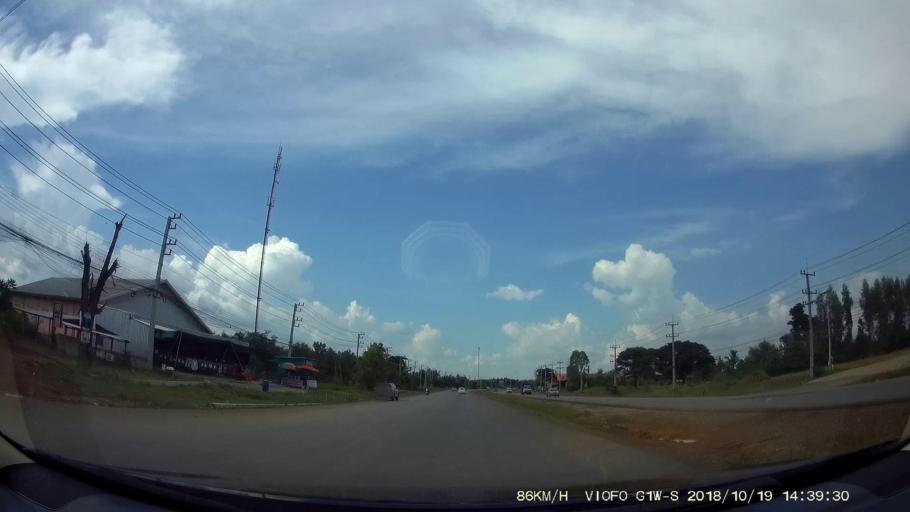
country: TH
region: Chaiyaphum
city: Kaeng Khro
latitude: 16.2269
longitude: 102.1949
